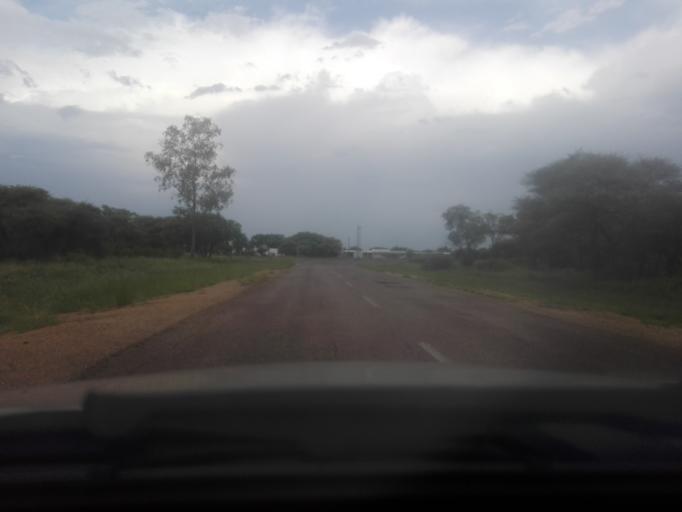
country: BW
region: Kweneng
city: Mmopone
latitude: -24.5577
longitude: 25.9273
